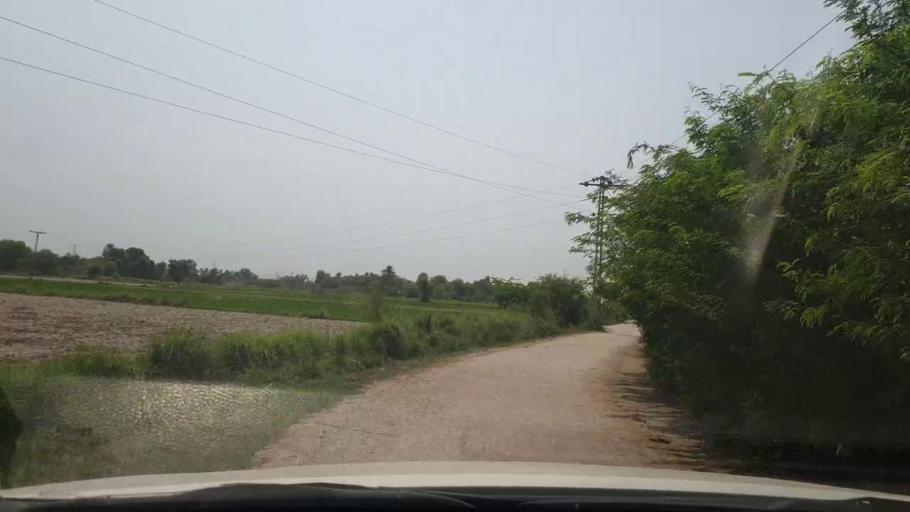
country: PK
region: Sindh
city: Shikarpur
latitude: 27.9901
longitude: 68.7126
